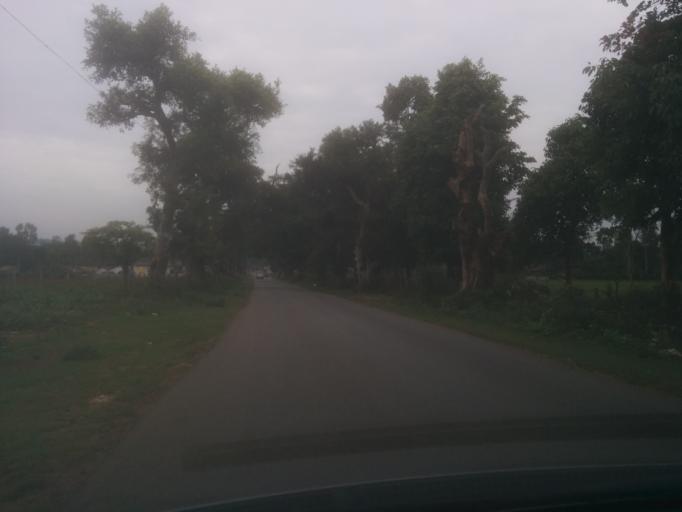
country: IN
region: Karnataka
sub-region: Chikmagalur
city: Chikmagalur
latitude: 13.3603
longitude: 75.7571
